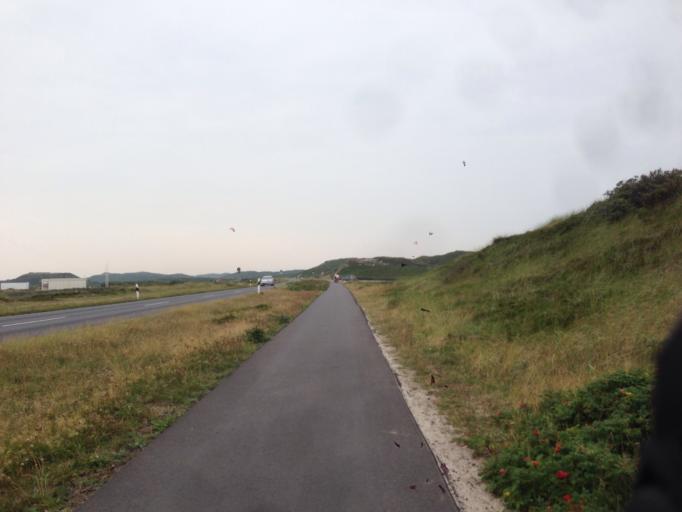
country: DE
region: Schleswig-Holstein
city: Westerland
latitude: 54.8120
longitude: 8.2893
